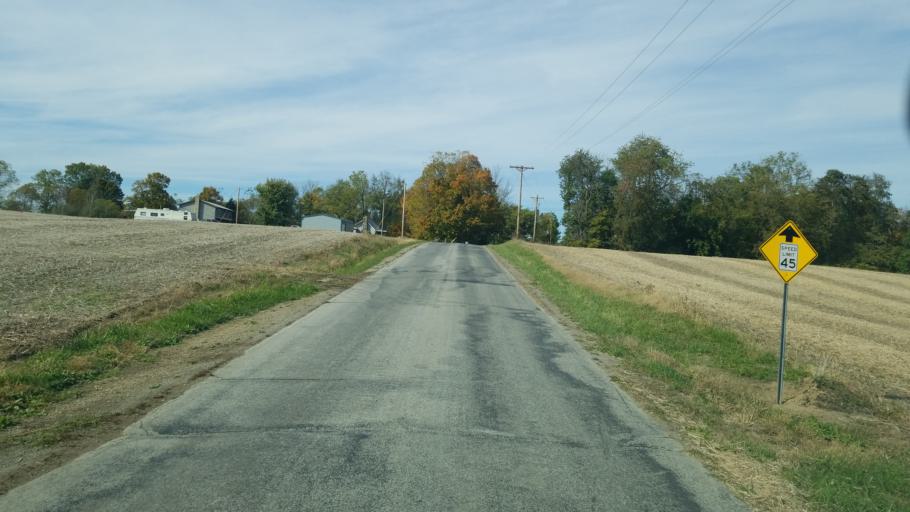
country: US
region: Ohio
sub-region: Highland County
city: Leesburg
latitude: 39.3201
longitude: -83.4717
